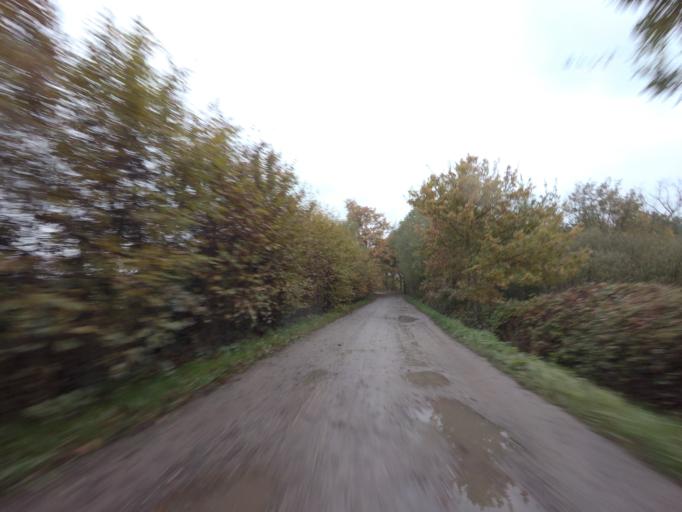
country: BE
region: Flanders
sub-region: Provincie Antwerpen
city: Bonheiden
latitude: 51.0086
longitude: 4.5710
